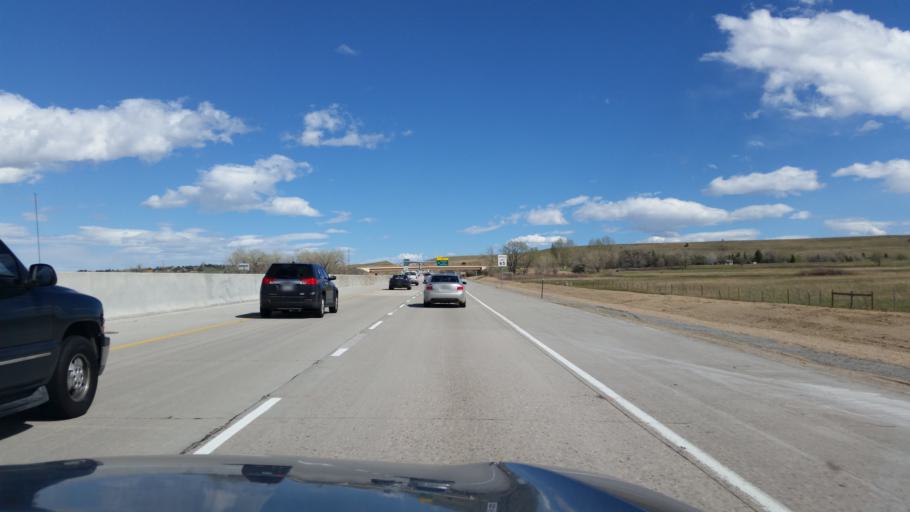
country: US
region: Colorado
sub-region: Boulder County
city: Superior
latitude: 39.9788
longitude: -105.2178
